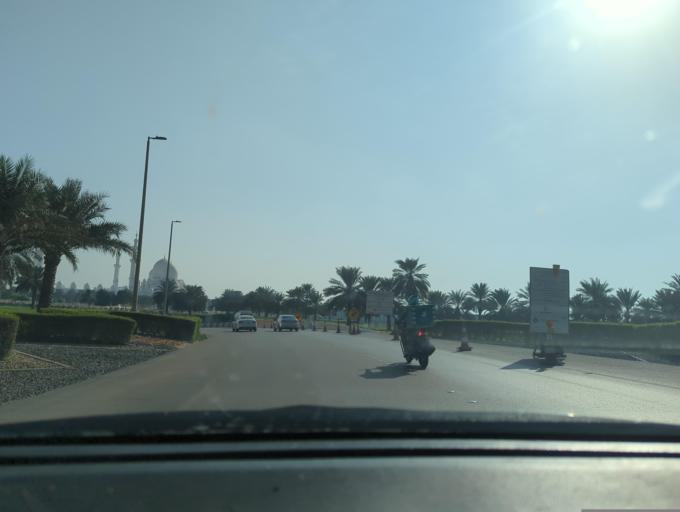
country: AE
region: Abu Dhabi
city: Abu Dhabi
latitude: 24.4209
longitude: 54.4743
